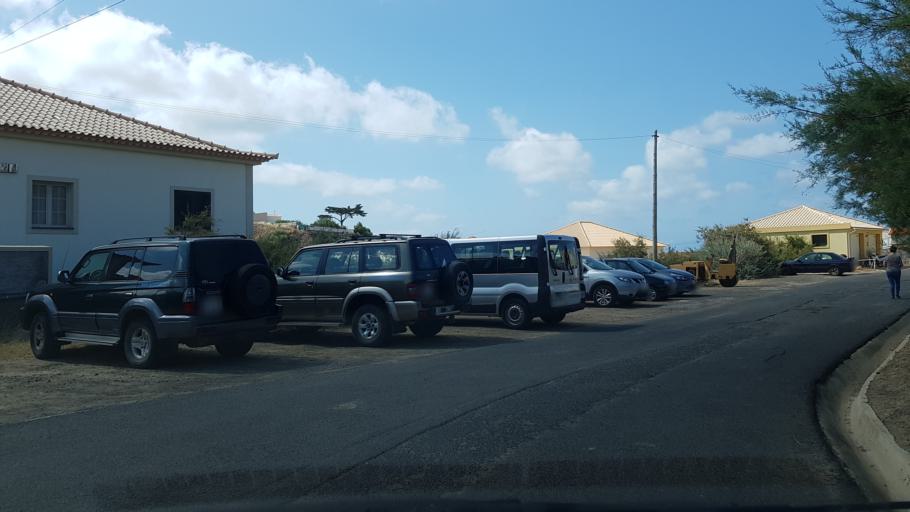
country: PT
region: Madeira
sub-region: Porto Santo
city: Vila de Porto Santo
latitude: 33.0652
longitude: -16.3325
